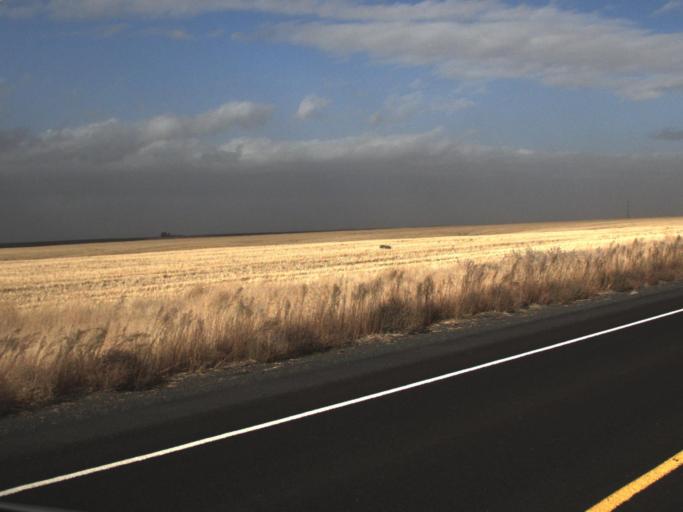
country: US
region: Washington
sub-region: Lincoln County
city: Davenport
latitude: 47.4359
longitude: -118.3329
